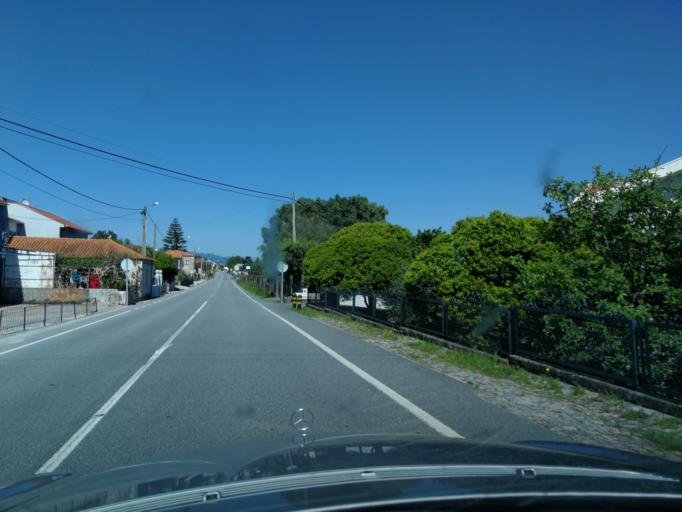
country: PT
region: Viana do Castelo
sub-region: Viana do Castelo
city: Darque
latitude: 41.7103
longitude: -8.7448
